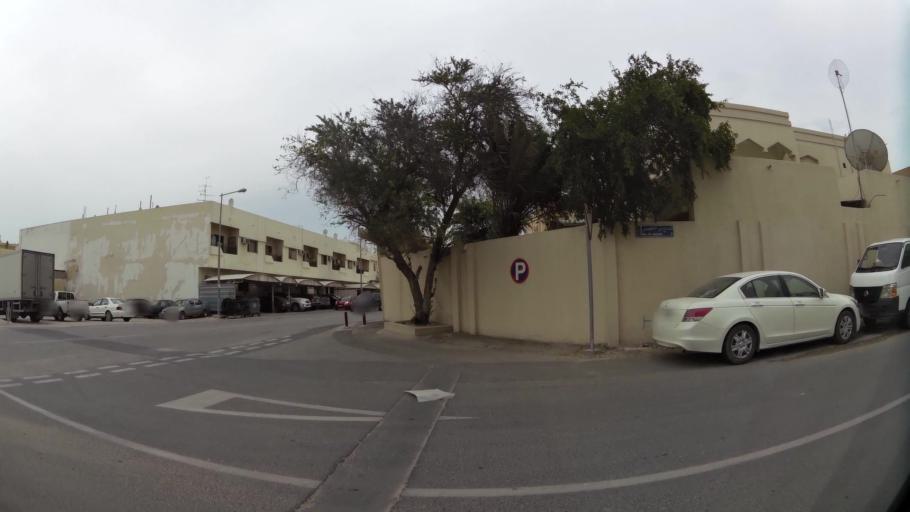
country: QA
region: Baladiyat ad Dawhah
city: Doha
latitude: 25.3114
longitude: 51.4934
